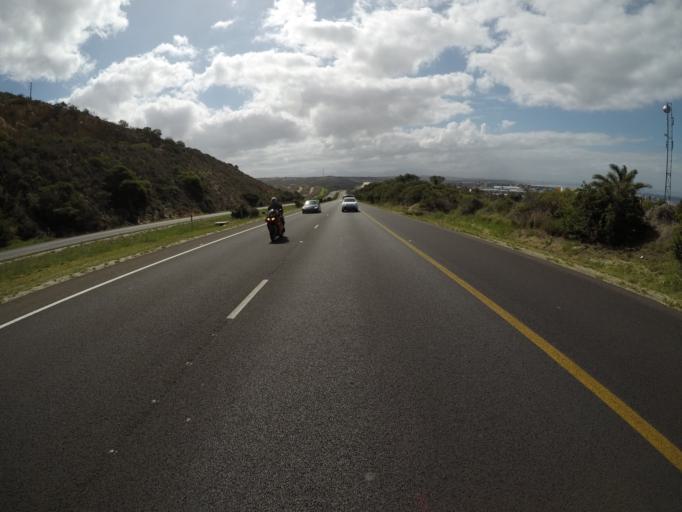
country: ZA
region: Western Cape
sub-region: Eden District Municipality
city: Mossel Bay
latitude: -34.1557
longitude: 22.0996
